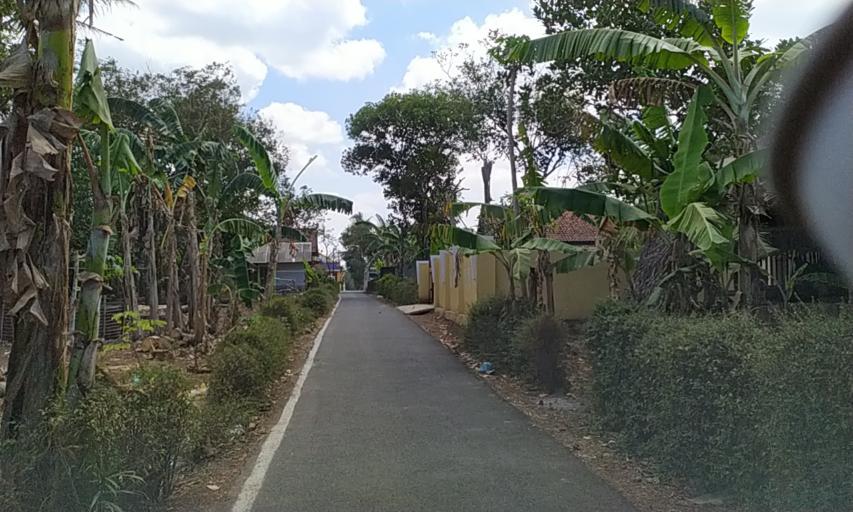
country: ID
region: Central Java
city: Kroya
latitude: -7.6396
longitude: 109.2332
